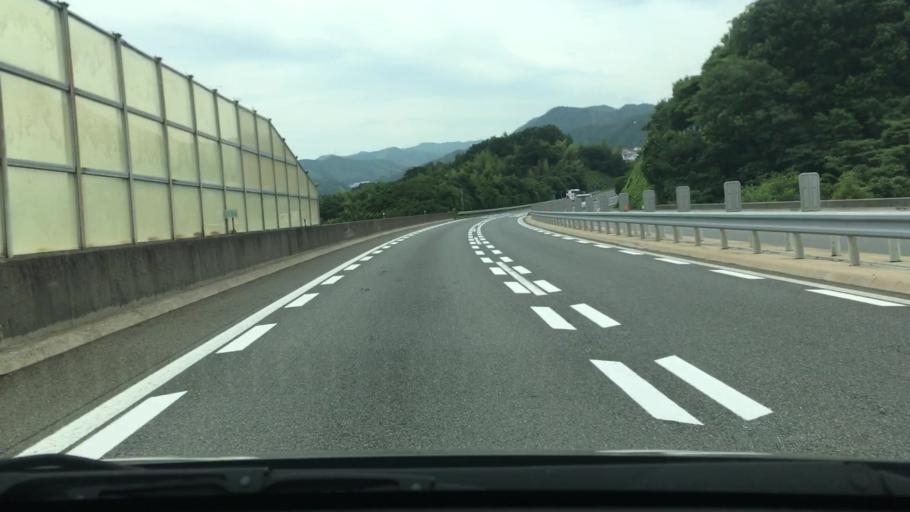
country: JP
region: Hiroshima
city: Ono-hara
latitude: 34.2664
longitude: 132.2411
